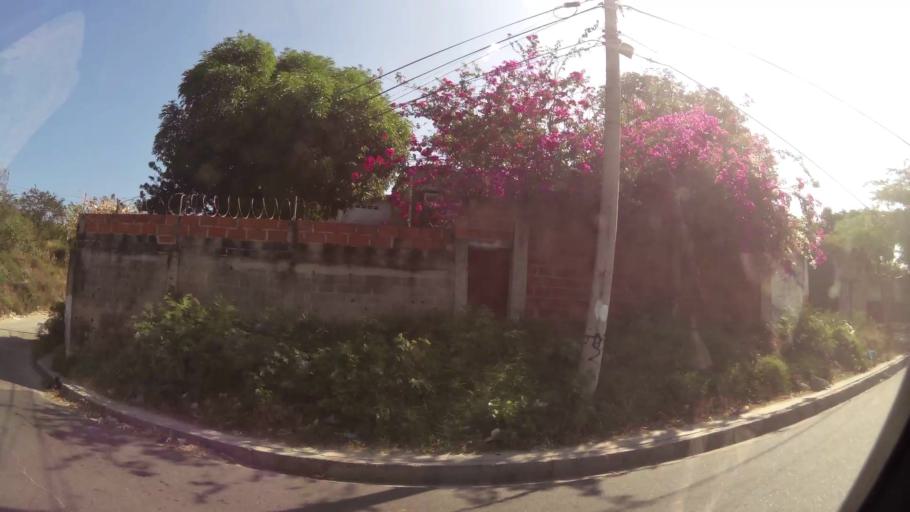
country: CO
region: Atlantico
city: Barranquilla
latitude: 10.9842
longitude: -74.8253
